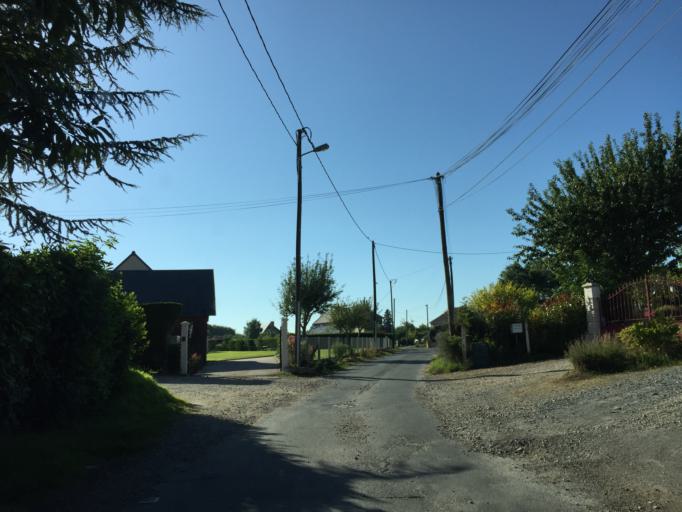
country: FR
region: Lower Normandy
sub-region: Departement du Calvados
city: Equemauville
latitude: 49.3936
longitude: 0.2040
